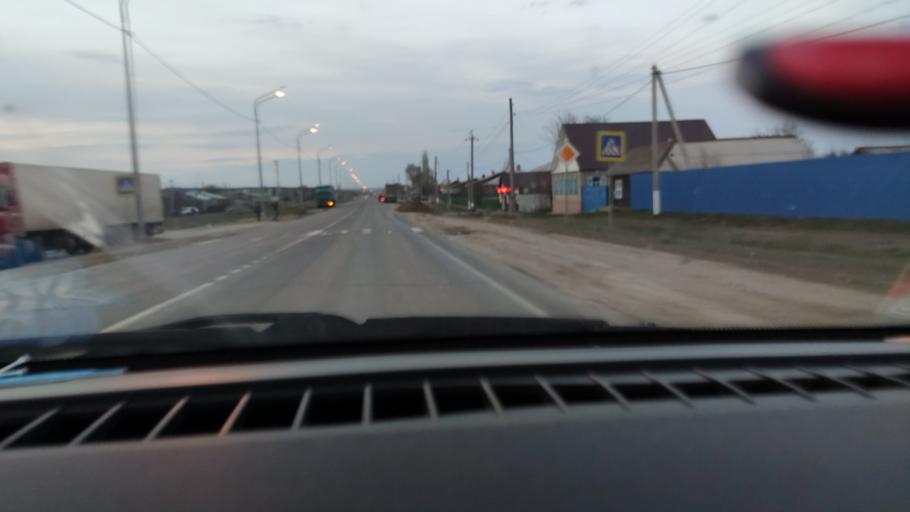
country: RU
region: Saratov
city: Sinodskoye
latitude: 51.9939
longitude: 46.6714
